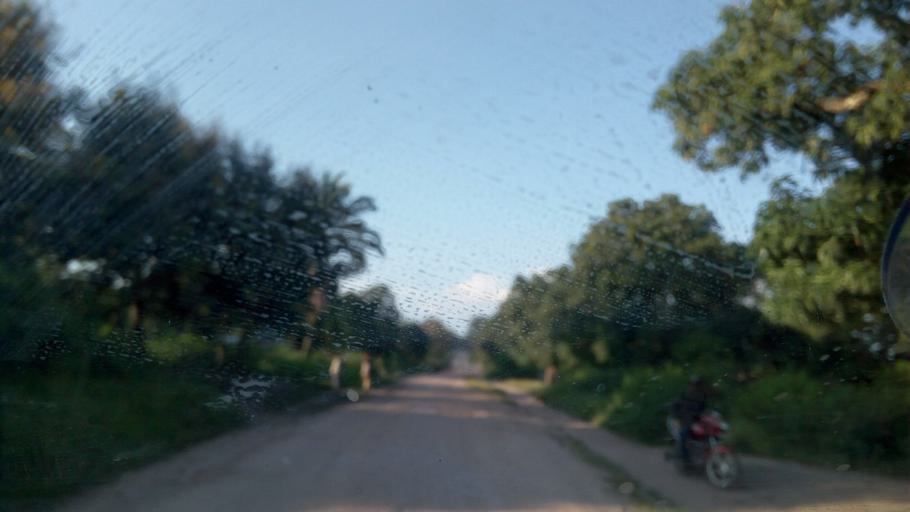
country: BI
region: Bururi
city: Rumonge
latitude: -4.1527
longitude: 29.0712
